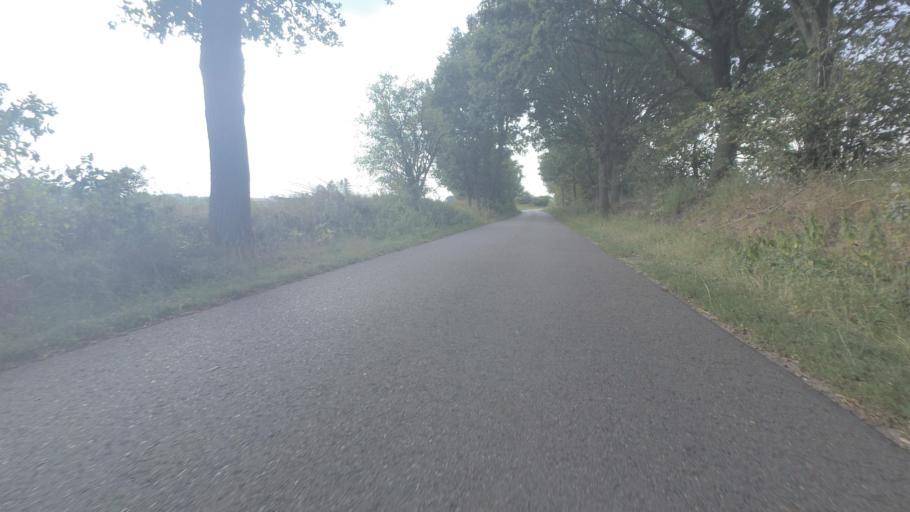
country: DE
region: Brandenburg
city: Wittstock
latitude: 53.2398
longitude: 12.4333
